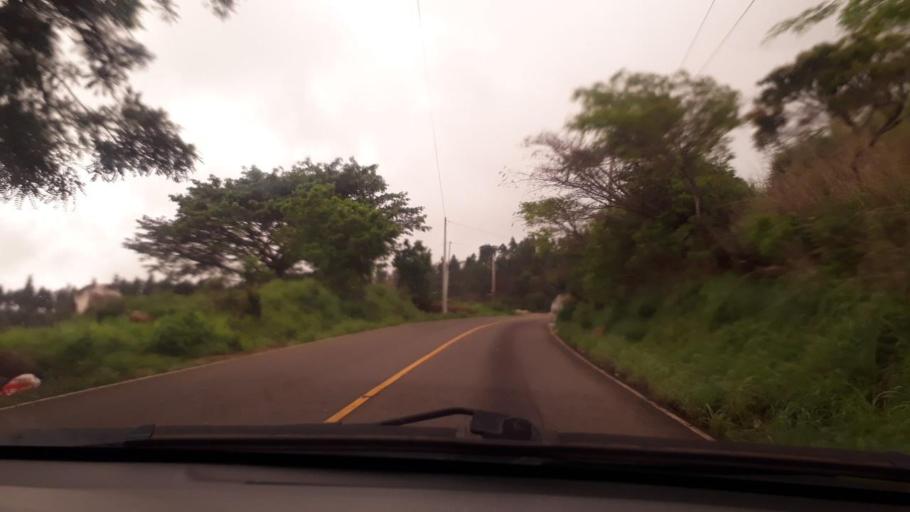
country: GT
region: Jutiapa
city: Moyuta
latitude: 14.0136
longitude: -90.0825
